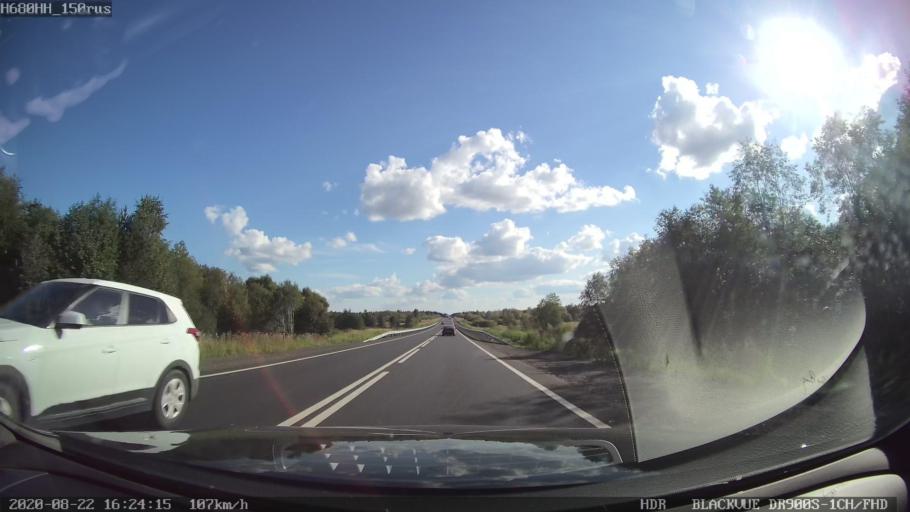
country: RU
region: Tverskaya
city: Rameshki
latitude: 57.3404
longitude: 36.0960
